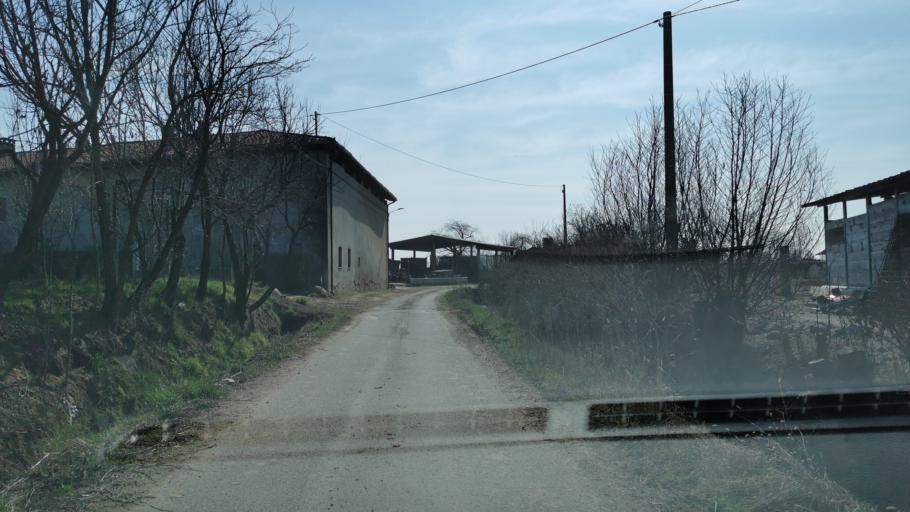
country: IT
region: Piedmont
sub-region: Provincia di Torino
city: Feletto
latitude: 45.2870
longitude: 7.7130
